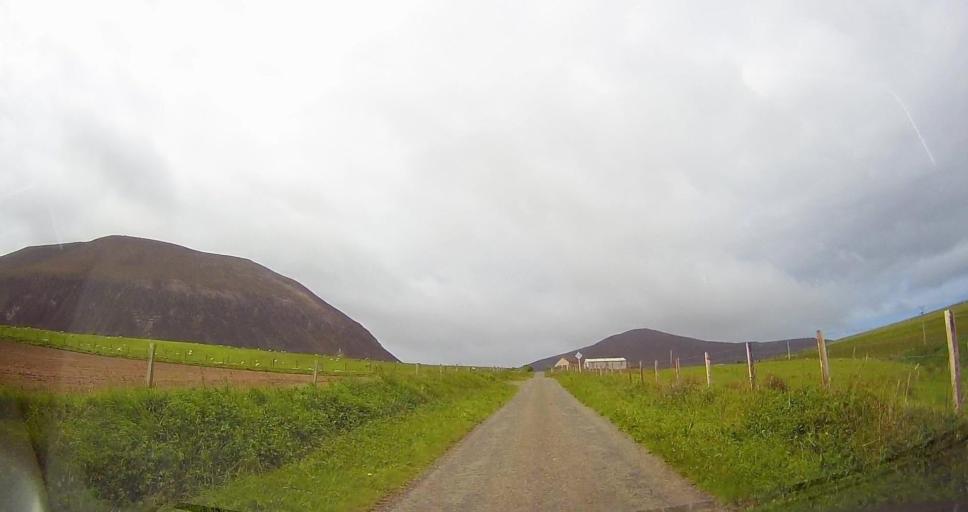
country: GB
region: Scotland
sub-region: Orkney Islands
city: Stromness
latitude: 58.9154
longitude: -3.3279
